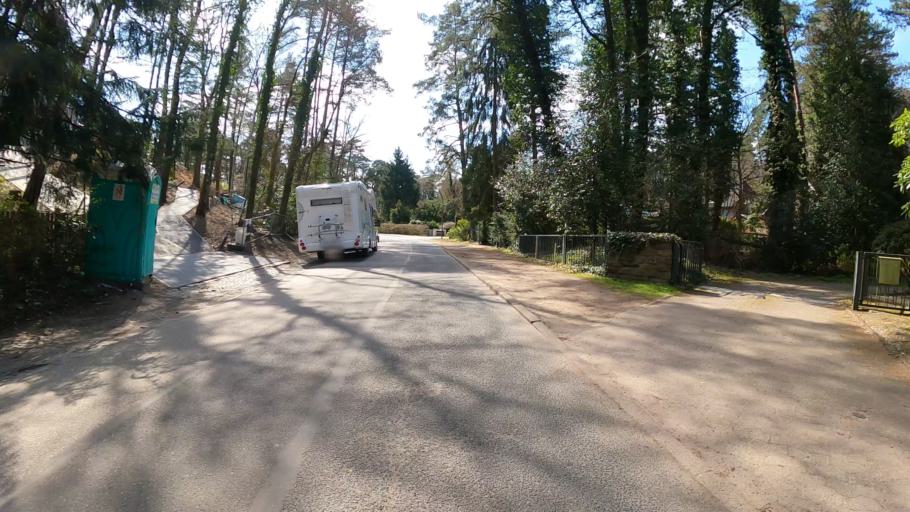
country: DE
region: Lower Saxony
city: Neu Wulmstorf
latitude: 53.4659
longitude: 9.8842
